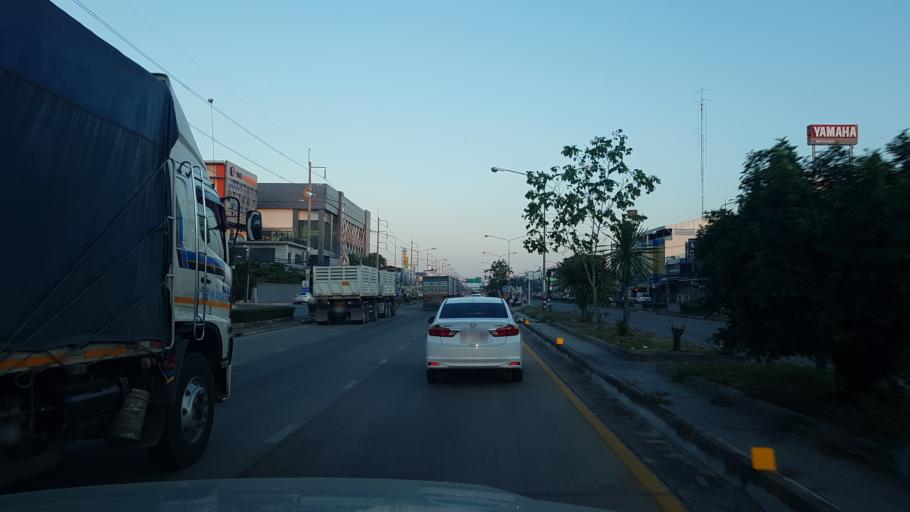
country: TH
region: Khon Kaen
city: Chum Phae
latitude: 16.5438
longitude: 102.1026
